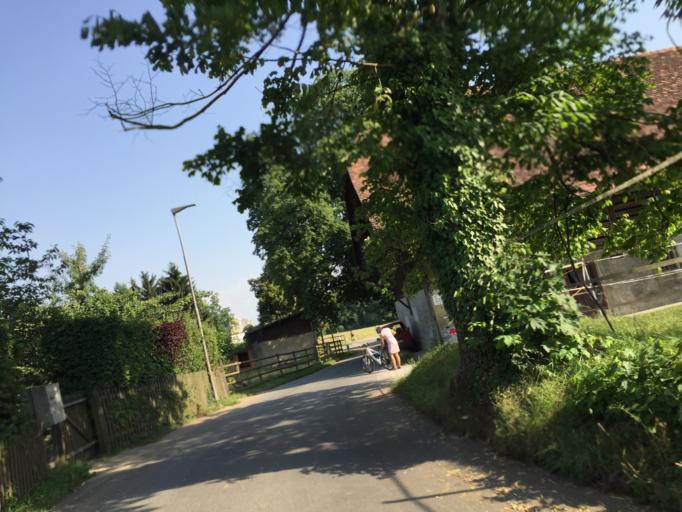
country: CH
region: Bern
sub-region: Bern-Mittelland District
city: Muri
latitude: 46.9428
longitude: 7.4826
